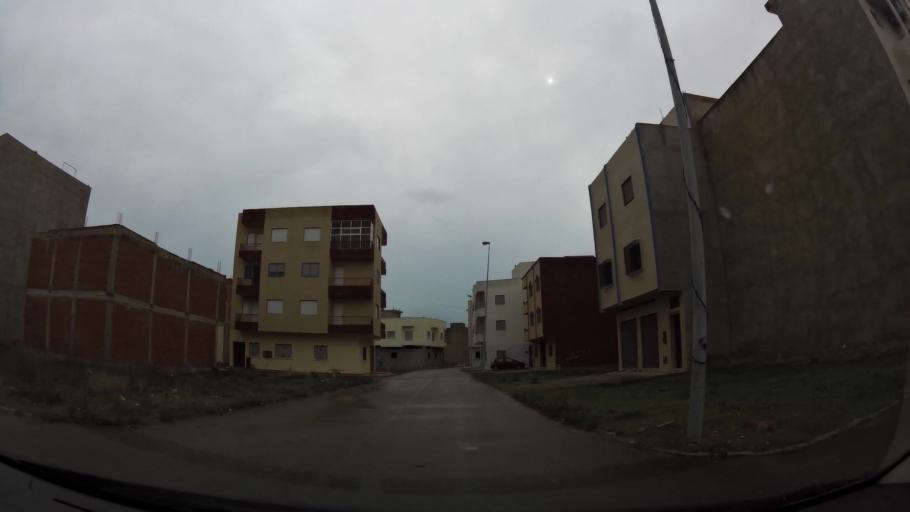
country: MA
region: Tanger-Tetouan
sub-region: Tetouan
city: Martil
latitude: 35.6138
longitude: -5.2991
